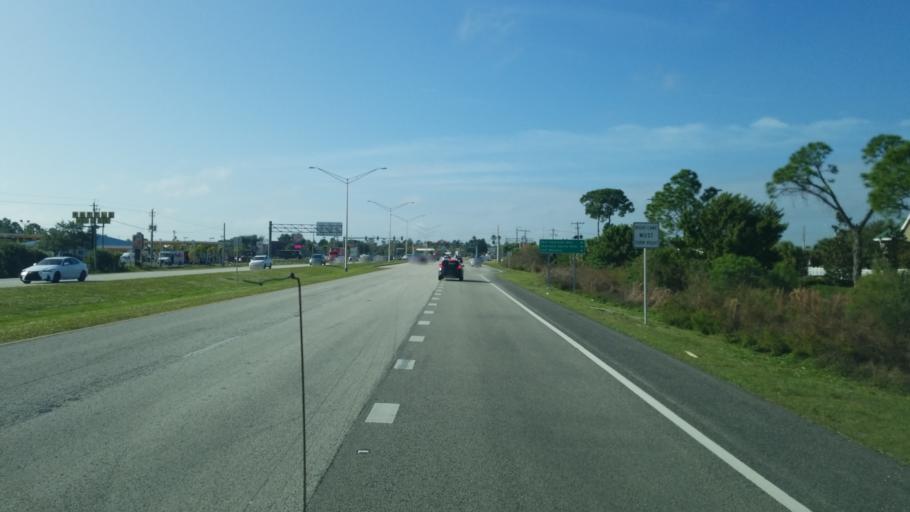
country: US
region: Florida
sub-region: Charlotte County
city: Harbour Heights
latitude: 27.0186
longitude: -82.0502
